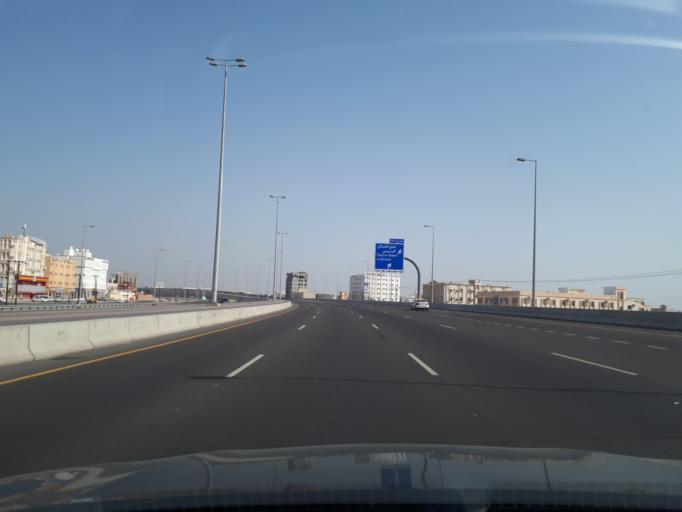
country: OM
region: Al Batinah
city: Al Liwa'
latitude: 24.4319
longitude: 56.6071
